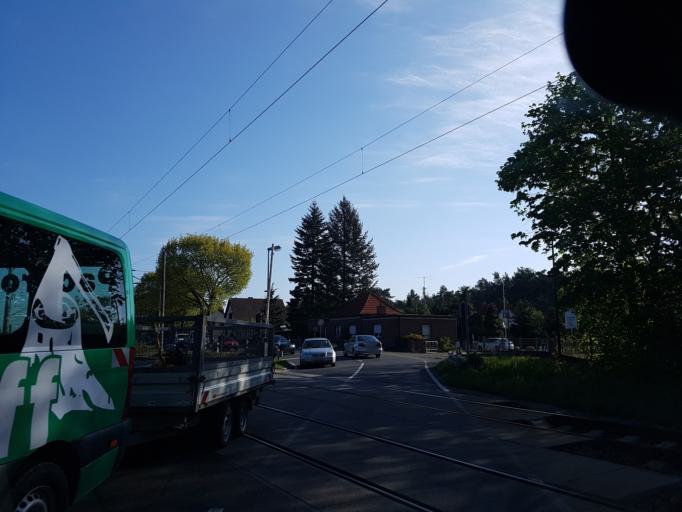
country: DE
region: Brandenburg
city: Grossraschen
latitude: 51.5977
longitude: 14.0148
